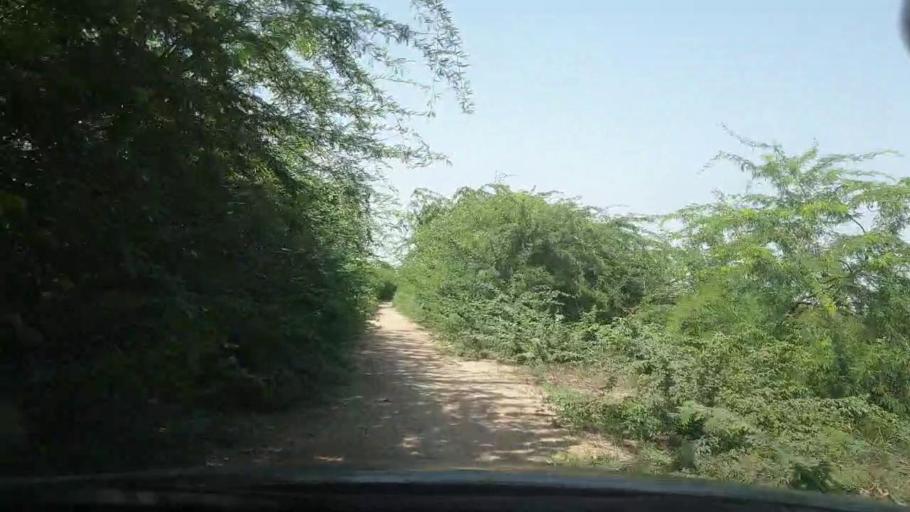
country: PK
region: Sindh
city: Naukot
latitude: 24.7992
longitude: 69.2639
